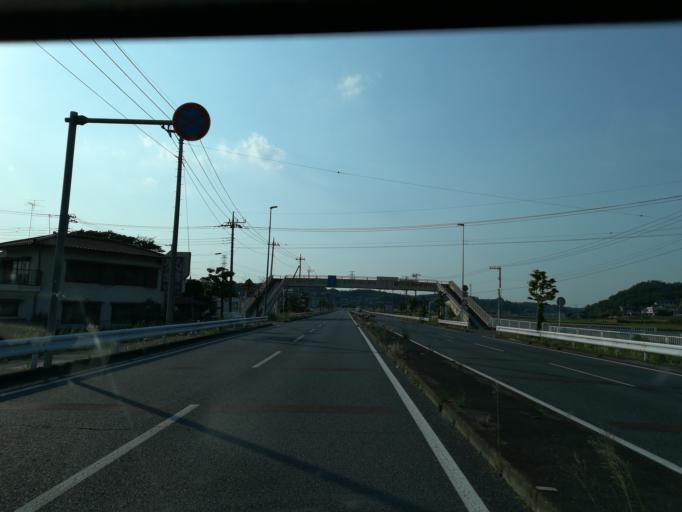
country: JP
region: Saitama
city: Kumagaya
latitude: 36.0692
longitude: 139.3616
